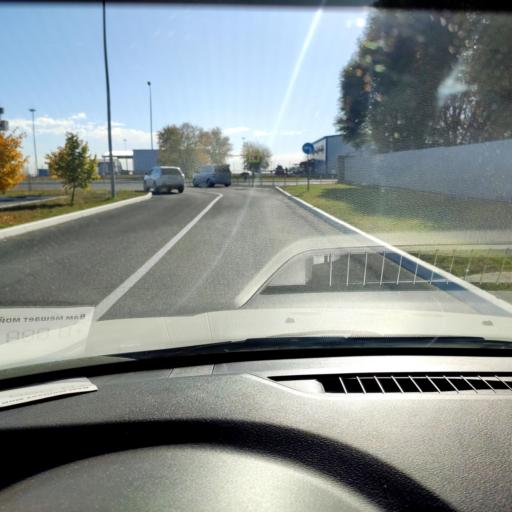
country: RU
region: Samara
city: Bereza
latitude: 53.5130
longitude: 50.1524
